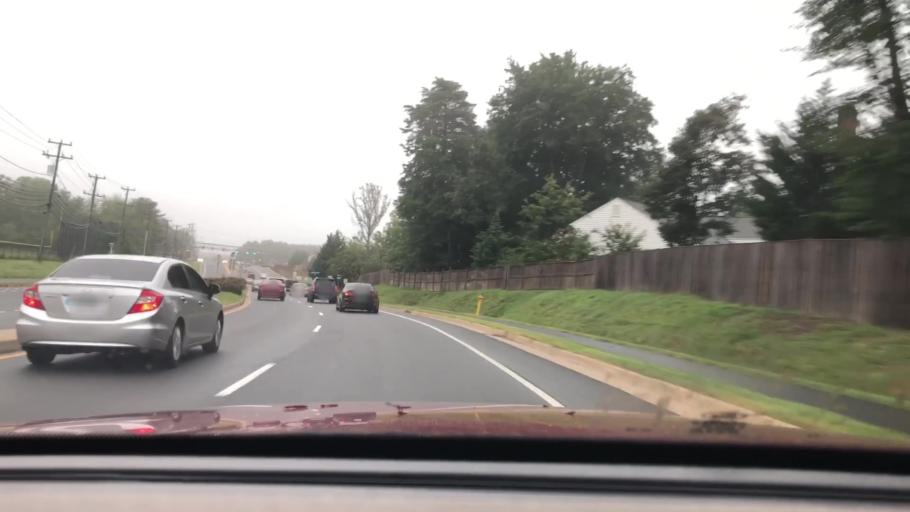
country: US
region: Virginia
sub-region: Fairfax County
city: Greenbriar
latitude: 38.8790
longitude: -77.4091
